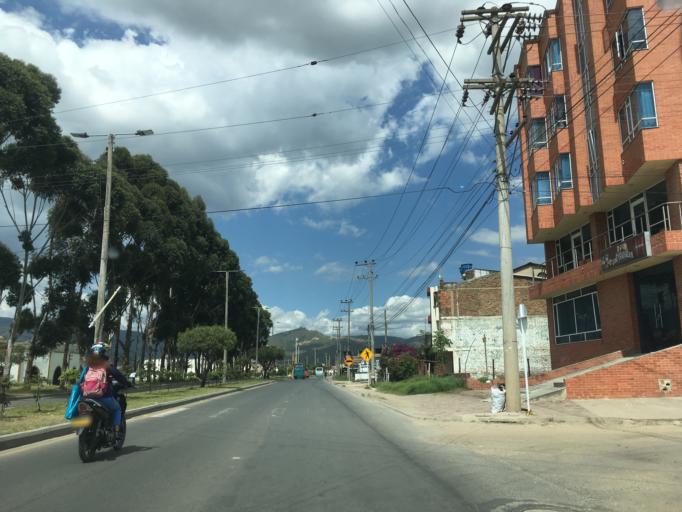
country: CO
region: Boyaca
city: Sogamoso
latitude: 5.7339
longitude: -72.9188
